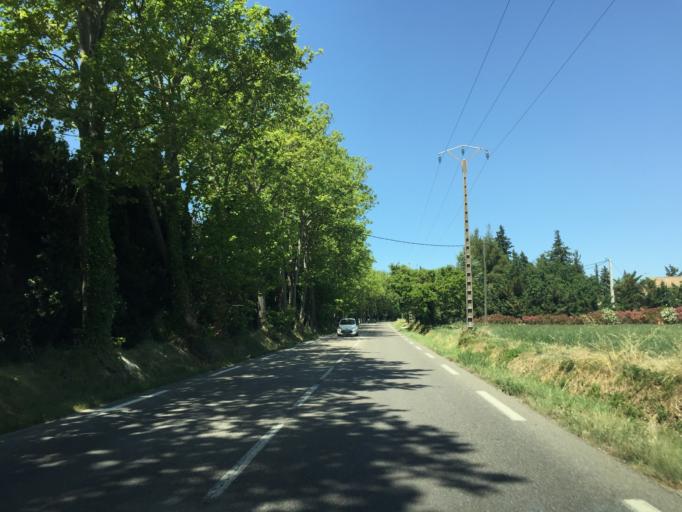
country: FR
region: Provence-Alpes-Cote d'Azur
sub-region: Departement du Vaucluse
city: Sarrians
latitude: 44.0937
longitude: 4.9514
